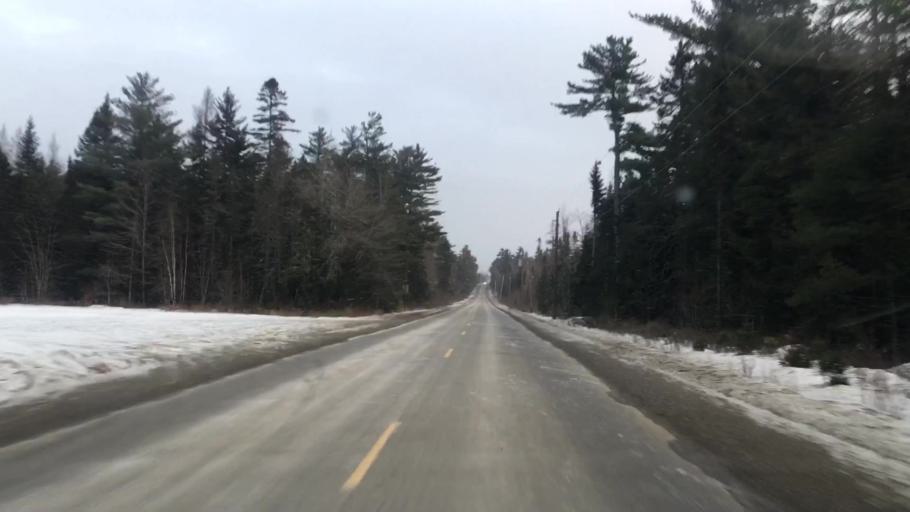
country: US
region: Maine
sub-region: Hancock County
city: Ellsworth
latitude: 44.6750
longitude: -68.3534
